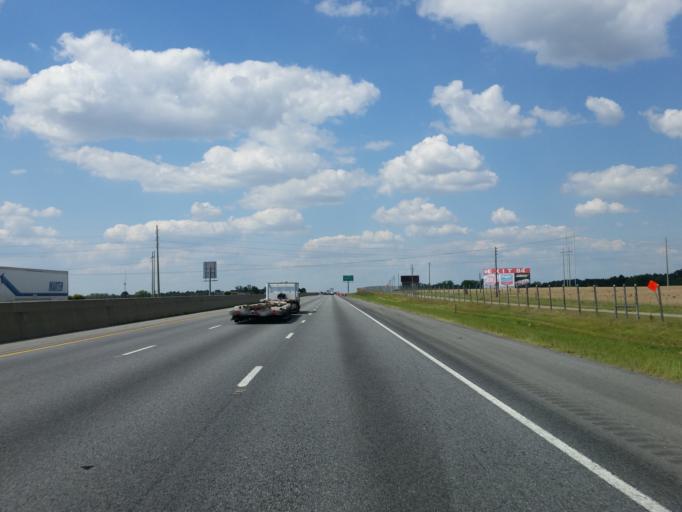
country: US
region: Georgia
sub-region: Tift County
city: Tifton
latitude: 31.4938
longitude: -83.5154
